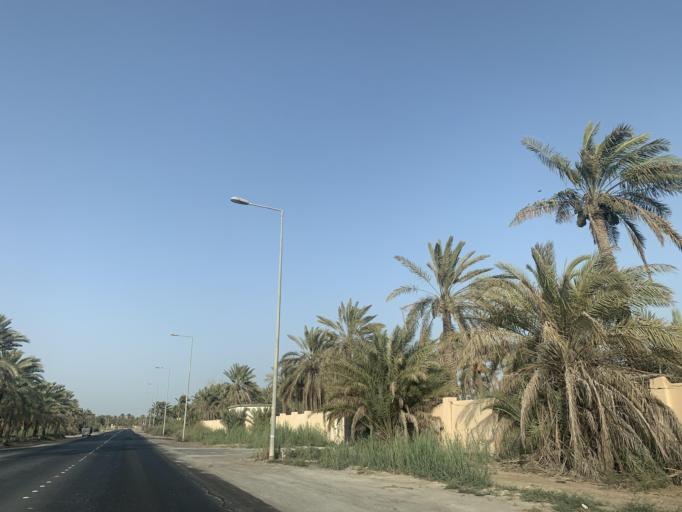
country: BH
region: Central Governorate
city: Madinat Hamad
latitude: 26.1753
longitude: 50.4545
